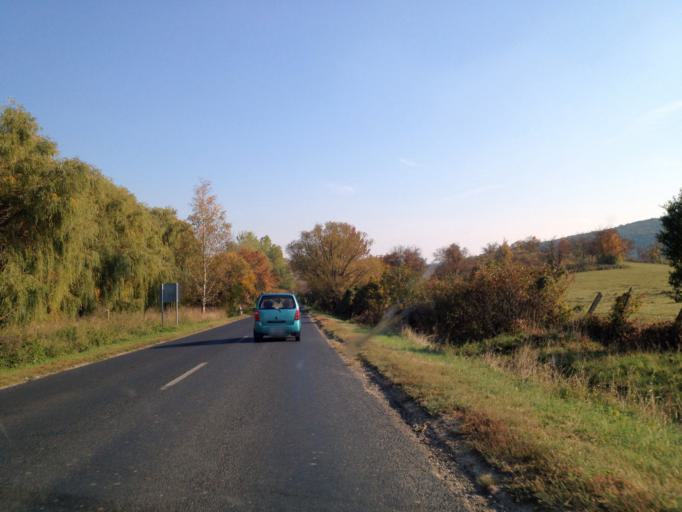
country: HU
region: Pest
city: Csobanka
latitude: 47.6623
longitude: 18.9719
